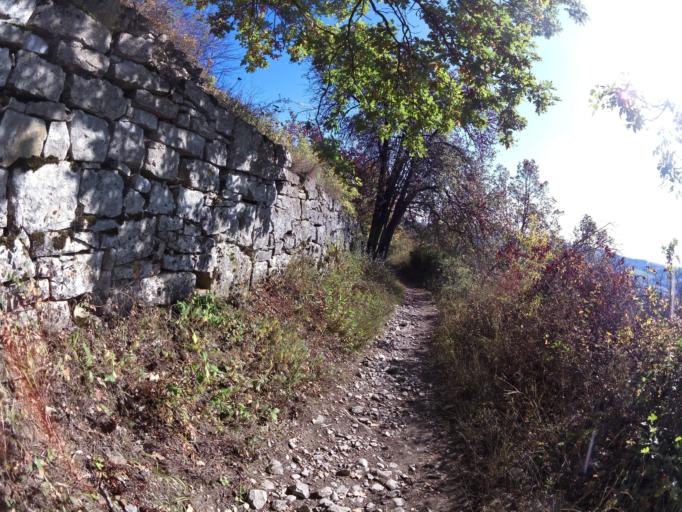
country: DE
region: Bavaria
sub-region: Regierungsbezirk Unterfranken
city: Sommerhausen
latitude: 49.6804
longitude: 10.0400
